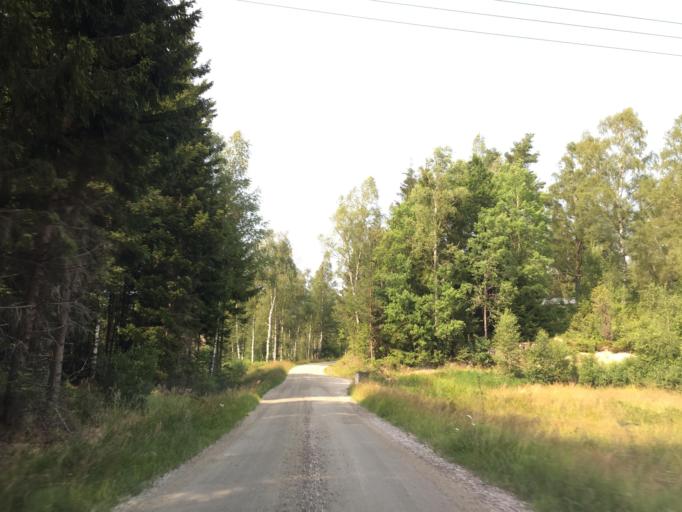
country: SE
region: Vaestra Goetaland
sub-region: Lilla Edets Kommun
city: Lilla Edet
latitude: 58.2428
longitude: 12.0824
